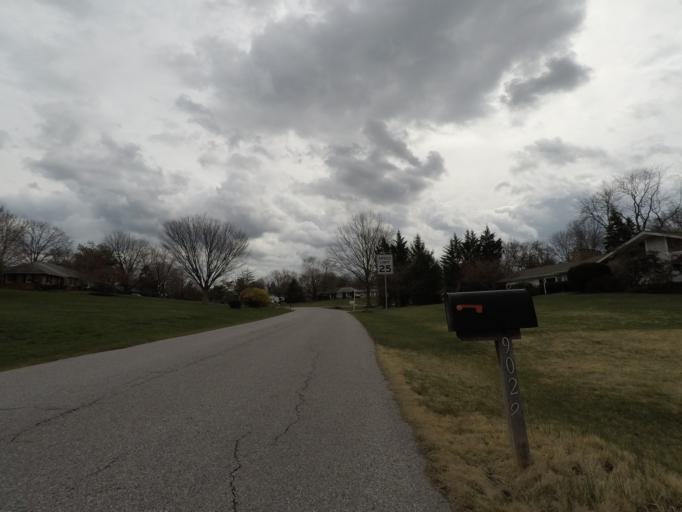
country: US
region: Maryland
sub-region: Howard County
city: Columbia
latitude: 39.2608
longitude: -76.8277
